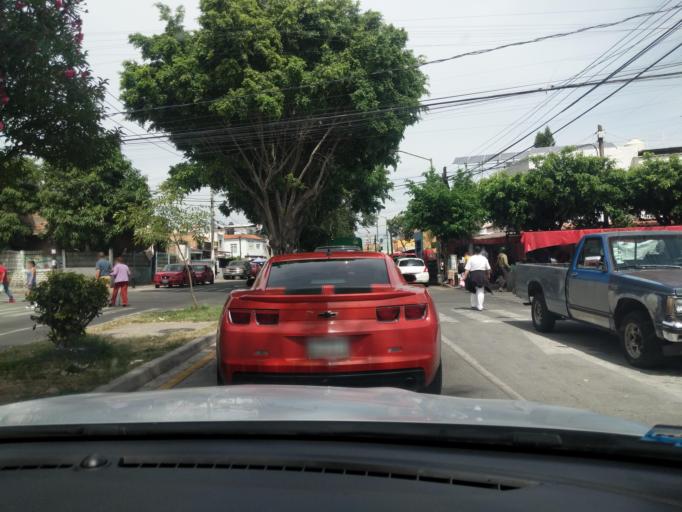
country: MX
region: Jalisco
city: Zapopan2
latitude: 20.7290
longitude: -103.4210
